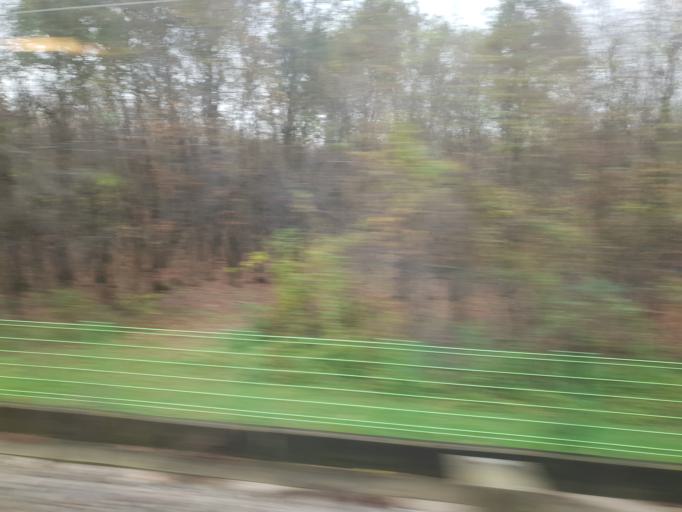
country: IT
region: Lombardy
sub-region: Citta metropolitana di Milano
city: Rescaldina
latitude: 45.6232
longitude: 8.9587
